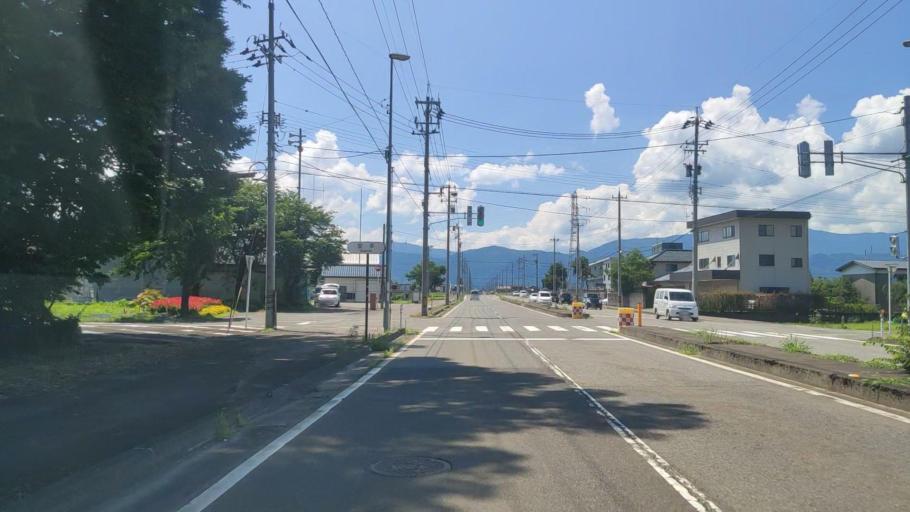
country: JP
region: Fukui
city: Ono
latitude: 35.9960
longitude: 136.5094
